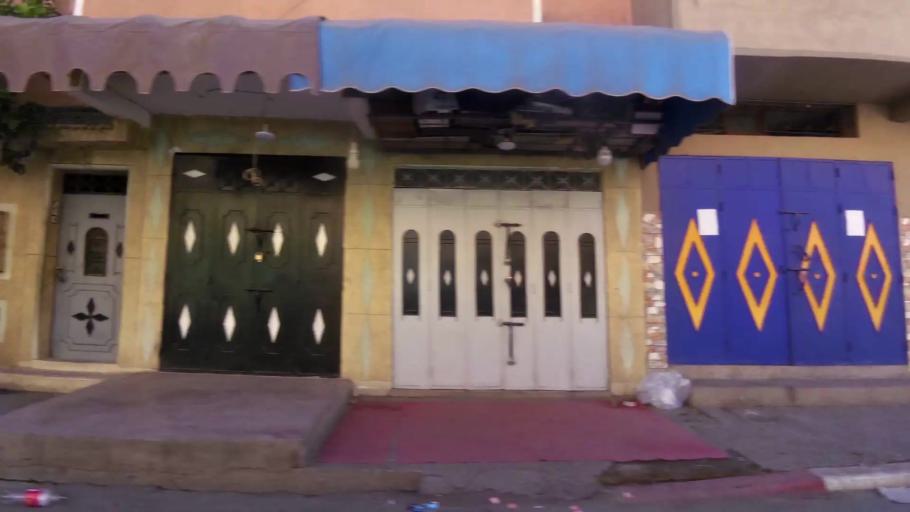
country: MA
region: Marrakech-Tensift-Al Haouz
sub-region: Marrakech
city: Marrakesh
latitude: 31.5950
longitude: -8.0302
